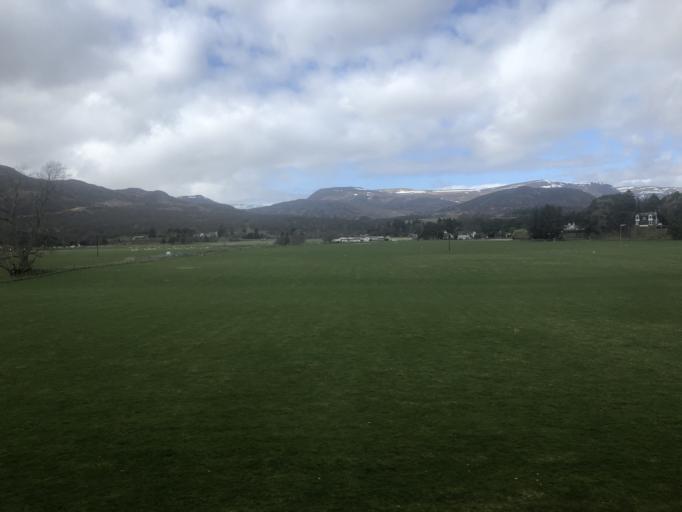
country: GB
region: Scotland
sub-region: Highland
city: Kingussie
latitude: 57.0568
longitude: -4.1224
